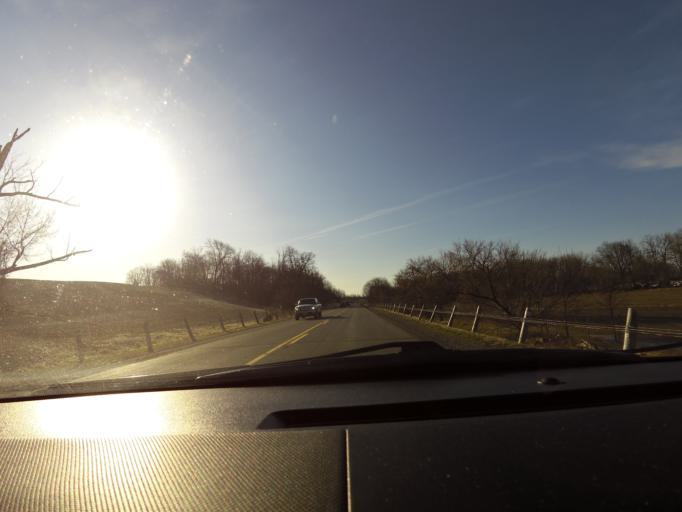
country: CA
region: Ontario
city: Ancaster
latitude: 43.0085
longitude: -79.8727
